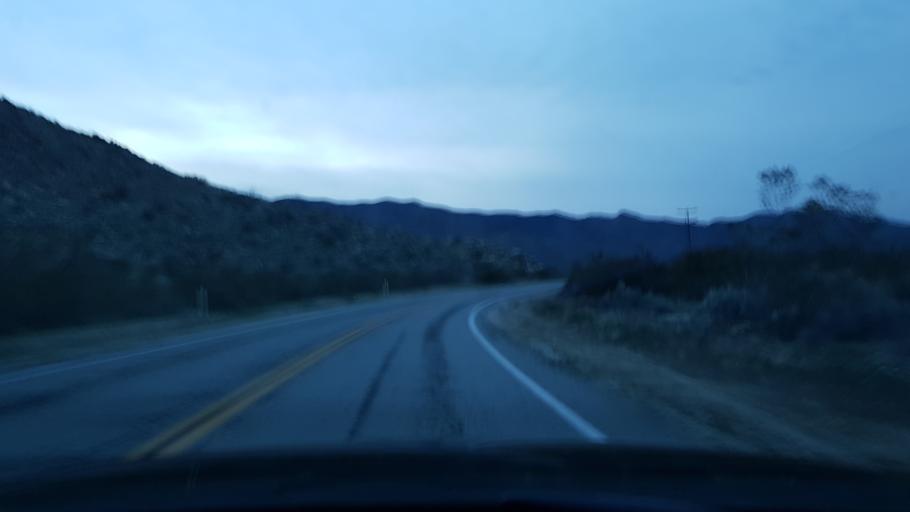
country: US
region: California
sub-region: San Diego County
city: Pine Valley
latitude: 32.9785
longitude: -116.4242
